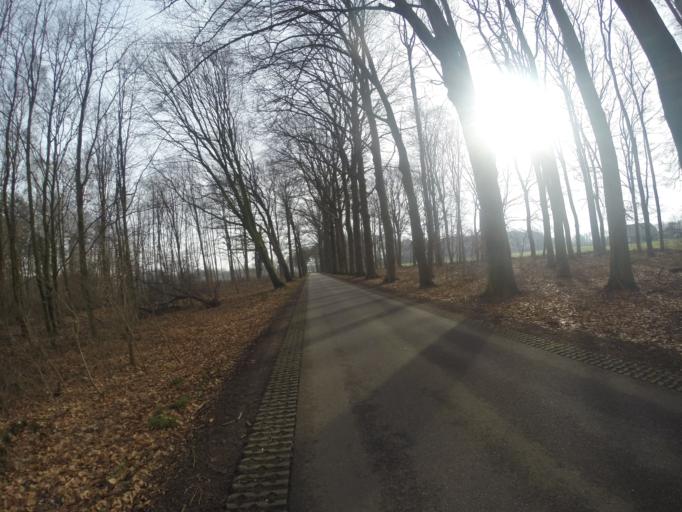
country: NL
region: Gelderland
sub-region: Gemeente Bronckhorst
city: Baak
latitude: 52.0905
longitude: 6.2753
